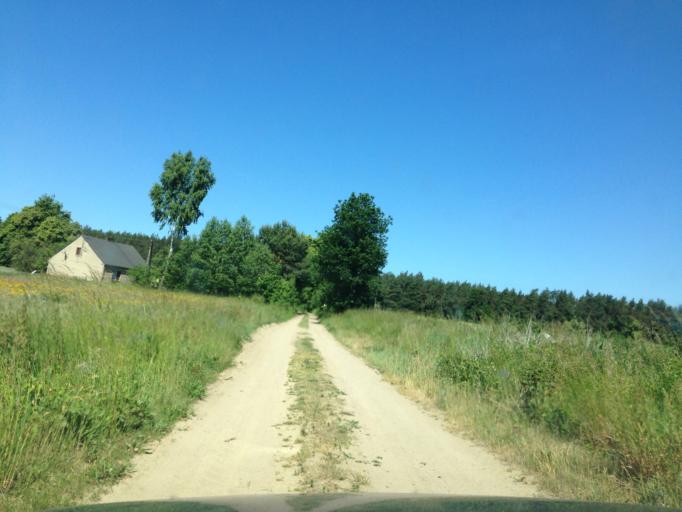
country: PL
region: Kujawsko-Pomorskie
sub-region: Powiat brodnicki
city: Bartniczka
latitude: 53.2619
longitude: 19.5846
